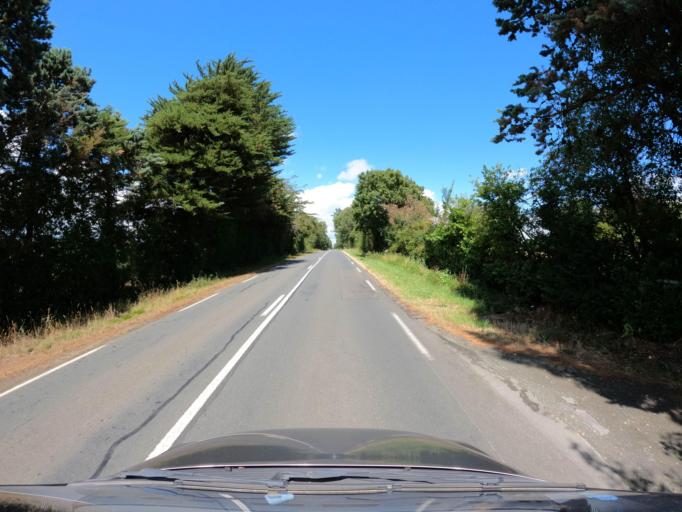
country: FR
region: Pays de la Loire
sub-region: Departement de la Sarthe
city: Brulon
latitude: 47.9321
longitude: -0.2601
